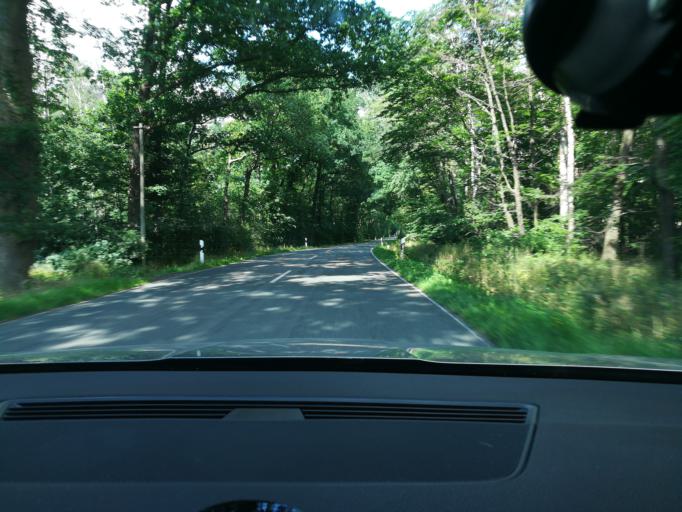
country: DE
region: North Rhine-Westphalia
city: Espelkamp
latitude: 52.3691
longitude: 8.6828
